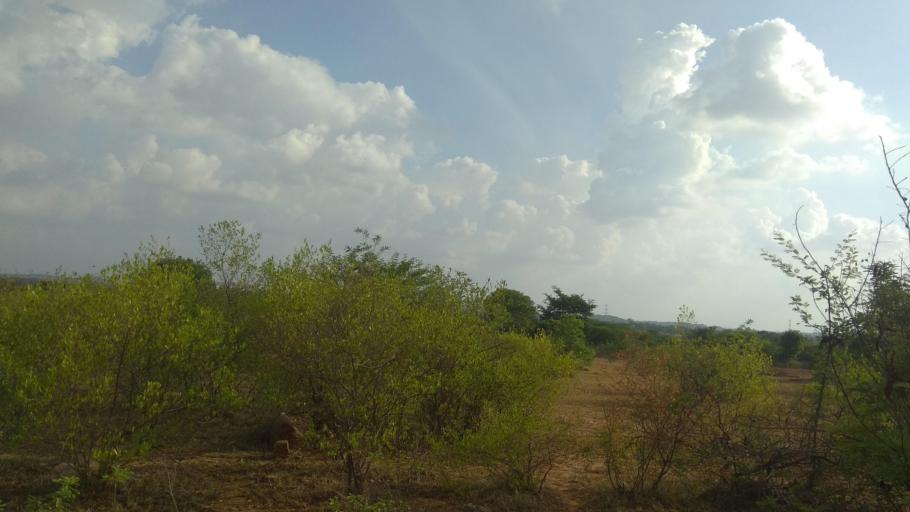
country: IN
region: Telangana
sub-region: Mahbubnagar
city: Farrukhnagar
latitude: 16.8875
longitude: 78.4785
